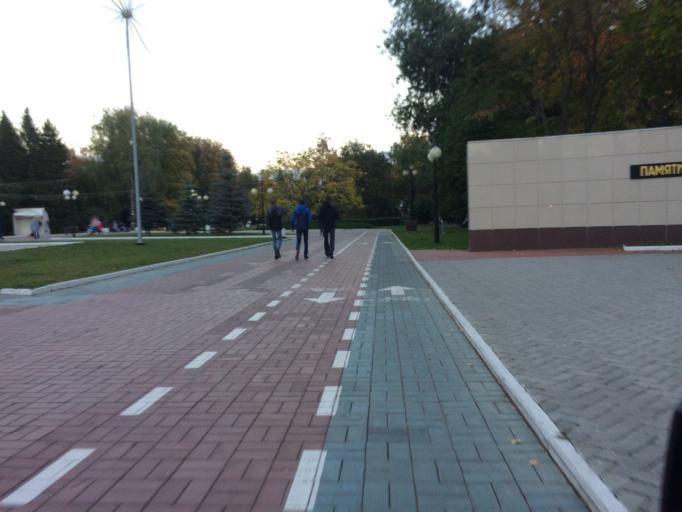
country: RU
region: Mariy-El
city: Yoshkar-Ola
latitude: 56.6366
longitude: 47.8886
